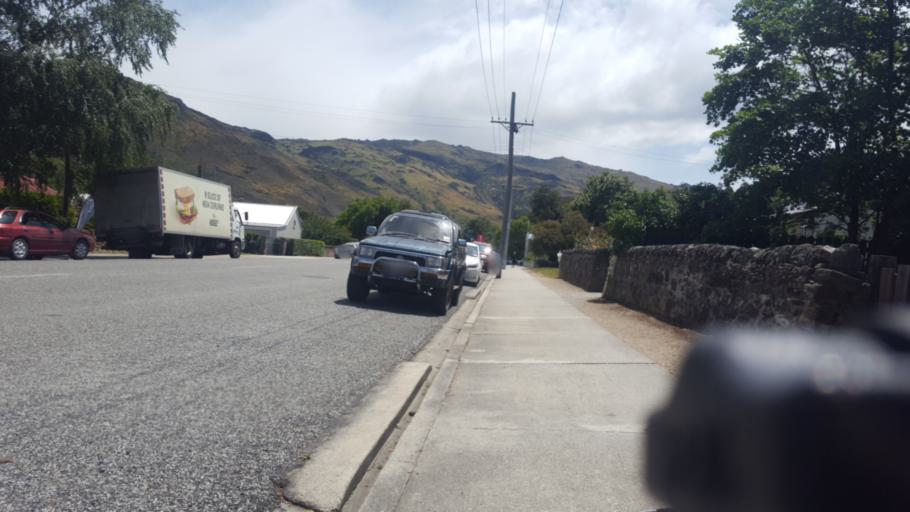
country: NZ
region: Otago
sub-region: Queenstown-Lakes District
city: Wanaka
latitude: -45.1881
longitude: 169.3183
